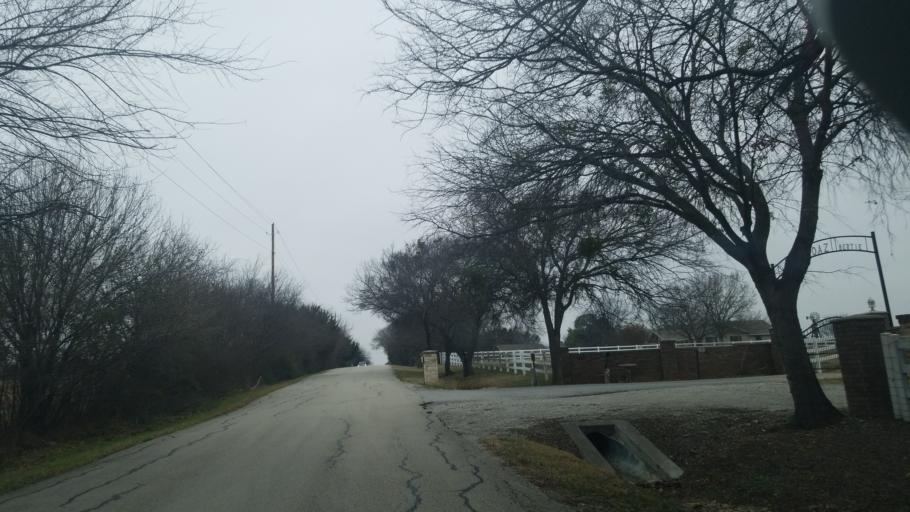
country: US
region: Texas
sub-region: Denton County
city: Argyle
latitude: 33.1473
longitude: -97.1593
